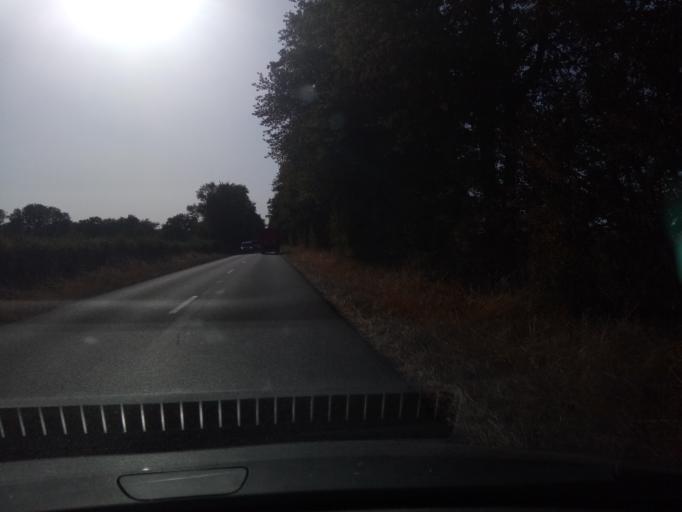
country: FR
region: Poitou-Charentes
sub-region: Departement de la Vienne
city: Montmorillon
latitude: 46.4445
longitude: 0.9684
